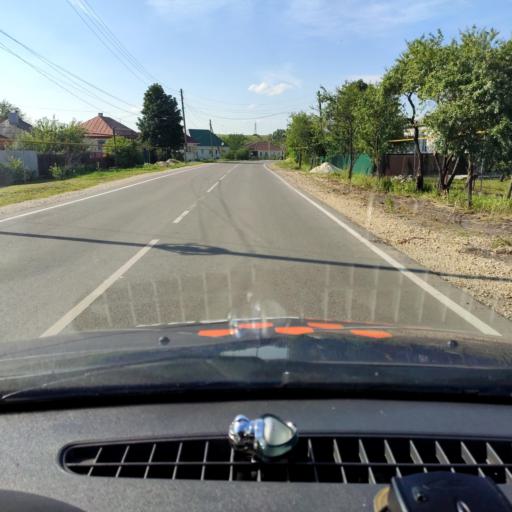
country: RU
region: Voronezj
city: Devitsa
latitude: 51.6546
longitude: 38.9711
